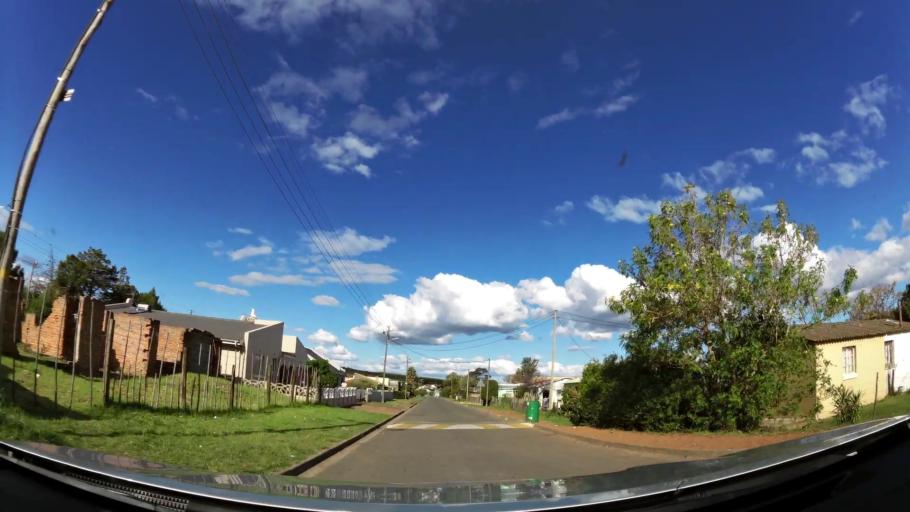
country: ZA
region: Western Cape
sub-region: Overberg District Municipality
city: Swellendam
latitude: -34.0348
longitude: 20.4414
